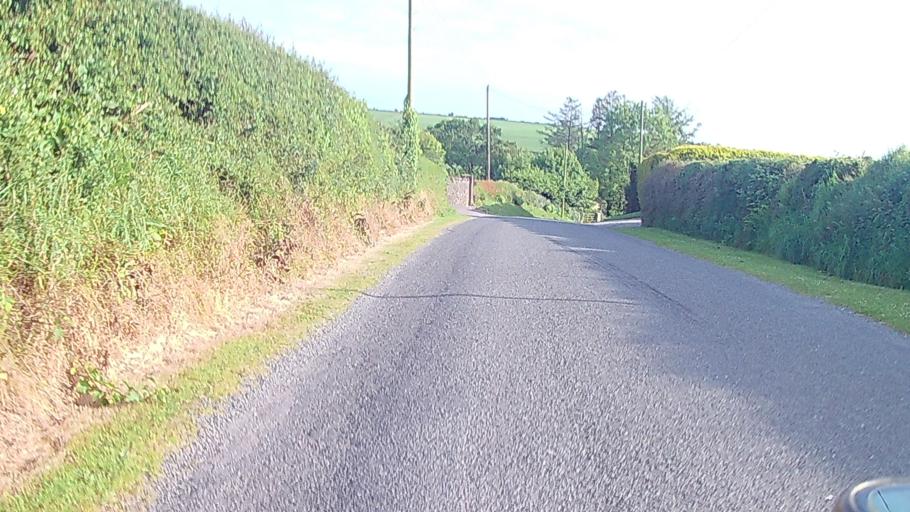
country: IE
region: Munster
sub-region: County Cork
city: Cork
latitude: 51.9789
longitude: -8.4582
